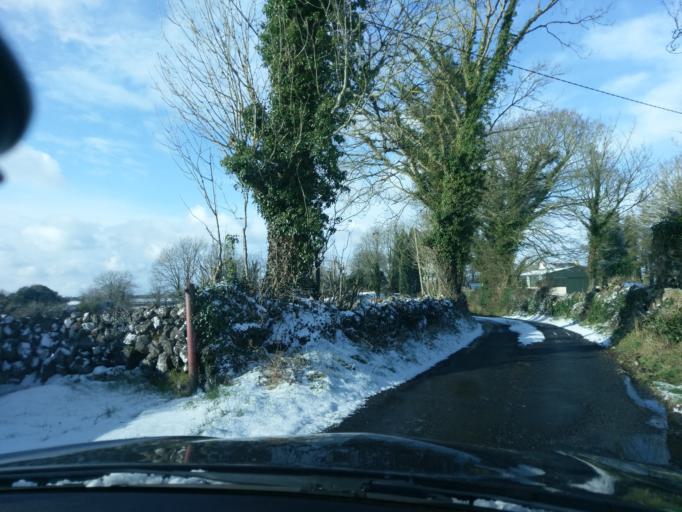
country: IE
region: Connaught
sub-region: County Galway
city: Athenry
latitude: 53.2059
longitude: -8.8128
